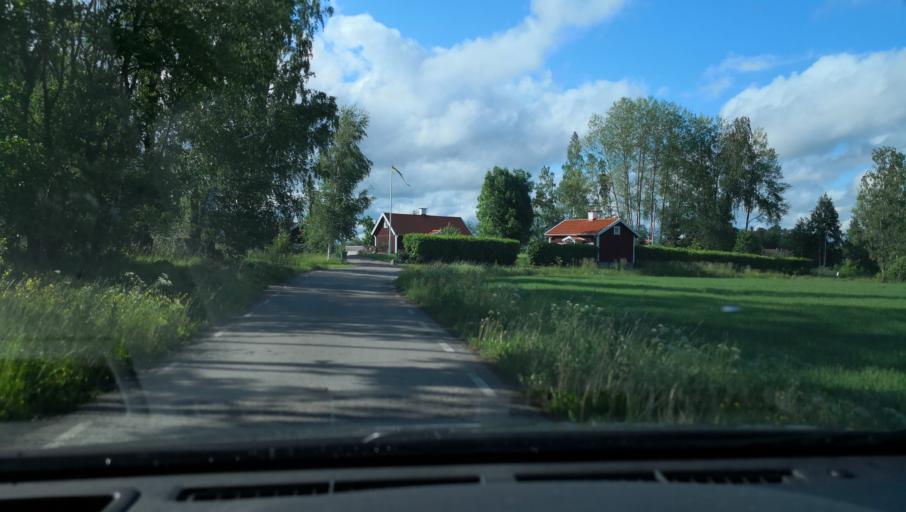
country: SE
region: OErebro
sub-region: Lindesbergs Kommun
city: Fellingsbro
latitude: 59.3347
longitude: 15.6853
